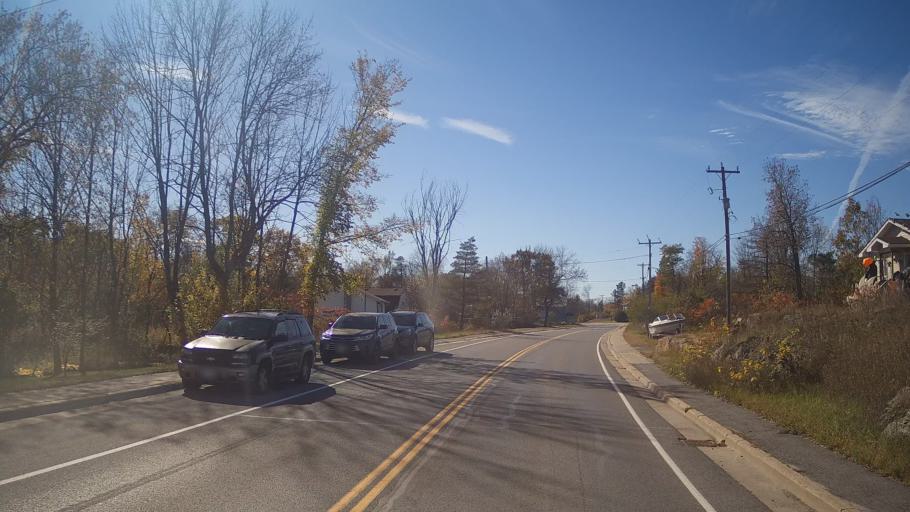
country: CA
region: Ontario
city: Kingston
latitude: 44.6626
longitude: -76.6790
